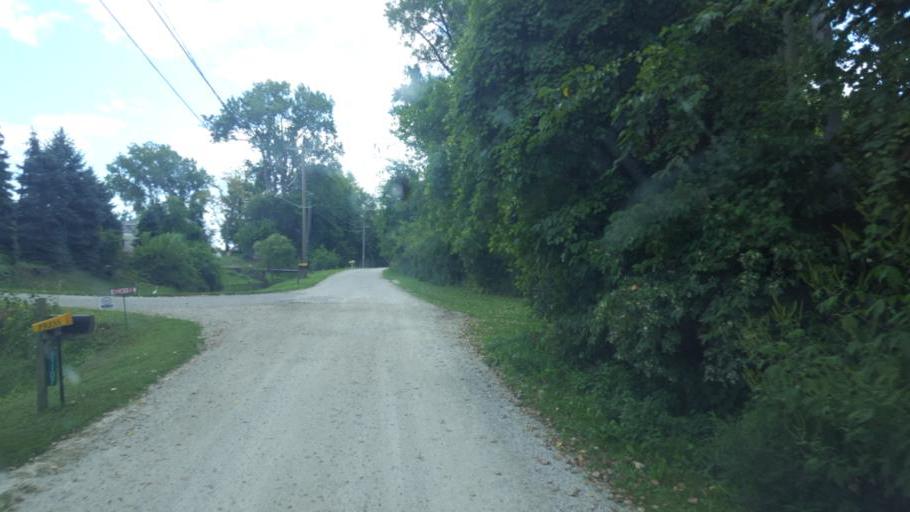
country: US
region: Ohio
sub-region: Lucas County
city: Curtice
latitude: 41.6733
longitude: -83.2810
